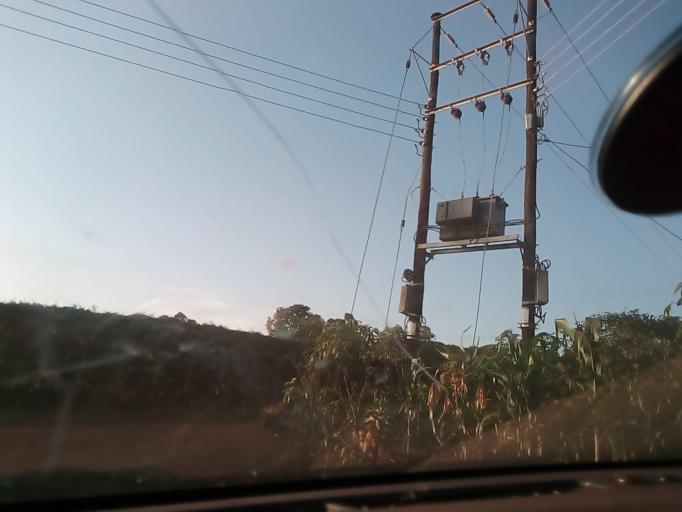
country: UG
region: Central Region
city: Masaka
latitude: -0.3376
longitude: 31.7595
